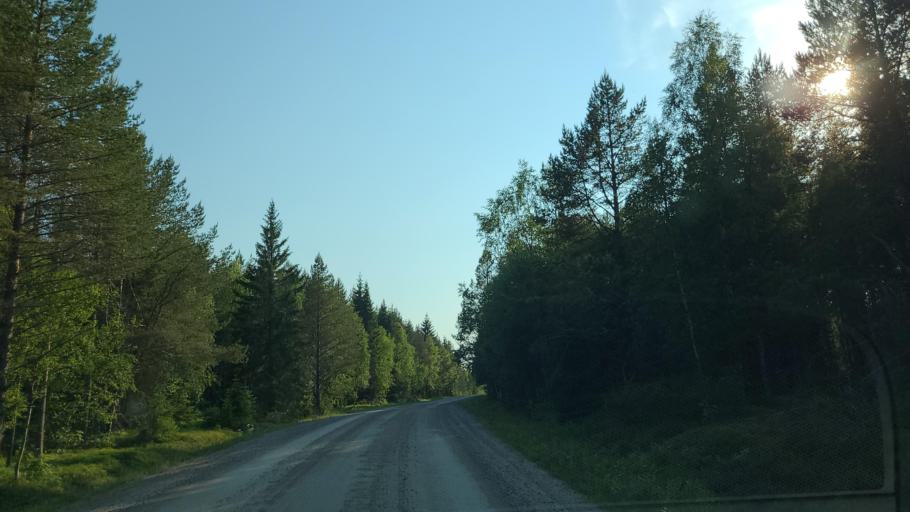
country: SE
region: Vaesterbotten
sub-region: Skelleftea Kommun
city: Burea
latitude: 64.3637
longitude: 21.4493
